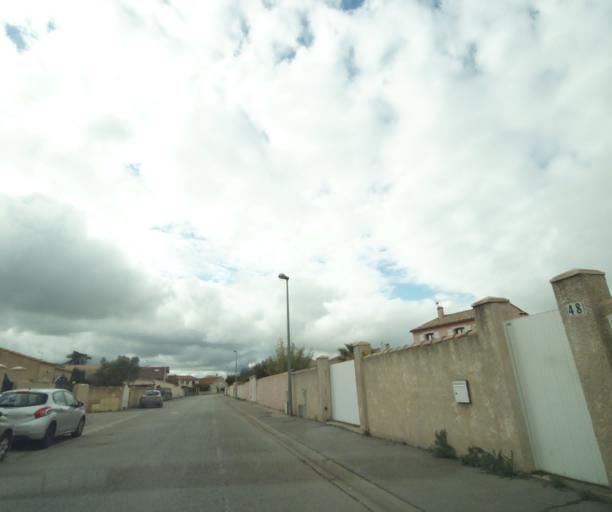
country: FR
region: Languedoc-Roussillon
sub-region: Departement de l'Herault
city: Fabregues
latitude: 43.5559
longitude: 3.7783
